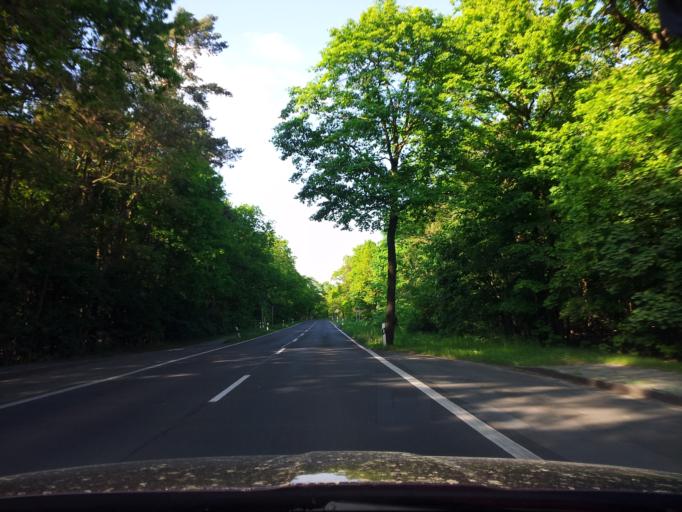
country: DE
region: Brandenburg
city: Juterbog
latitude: 52.0416
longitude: 13.1165
